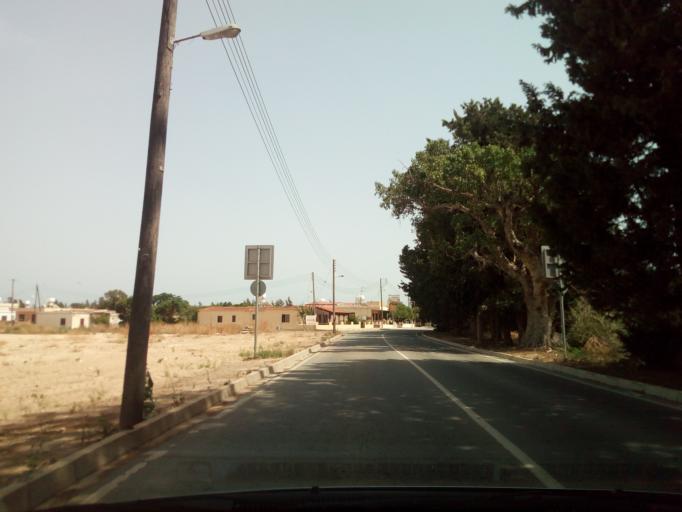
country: CY
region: Larnaka
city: Meneou
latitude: 34.8608
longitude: 33.5957
